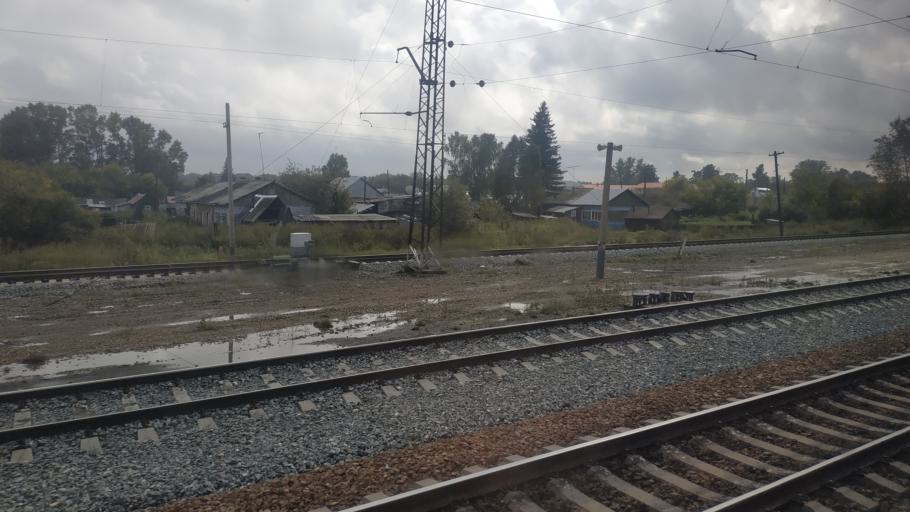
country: RU
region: Novosibirsk
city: Stantsionno-Oyashinskiy
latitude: 55.4641
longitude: 83.8245
